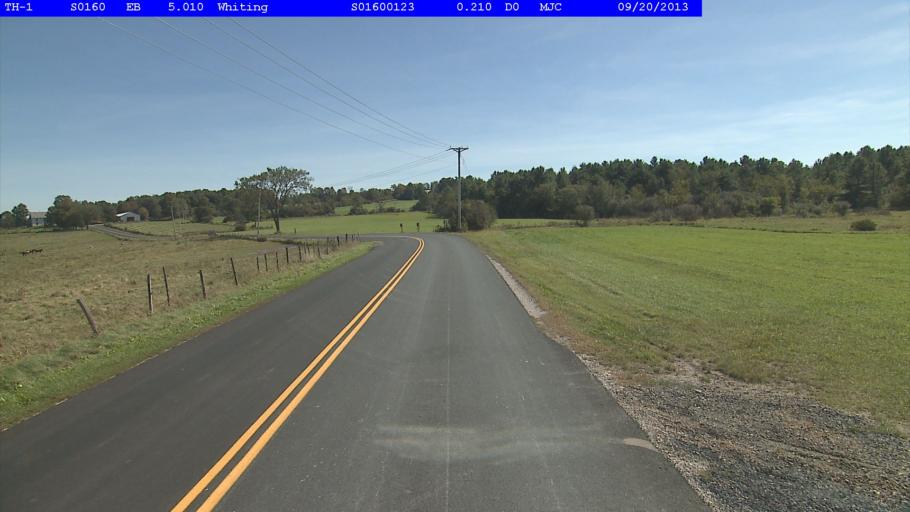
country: US
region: Vermont
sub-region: Rutland County
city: Brandon
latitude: 43.8624
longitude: -73.2212
